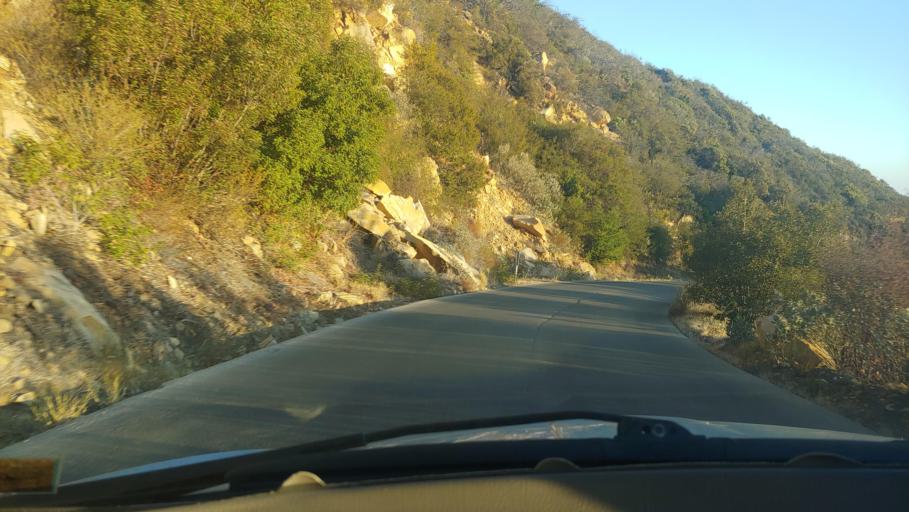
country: US
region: California
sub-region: Santa Barbara County
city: Mission Canyon
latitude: 34.4800
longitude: -119.6812
